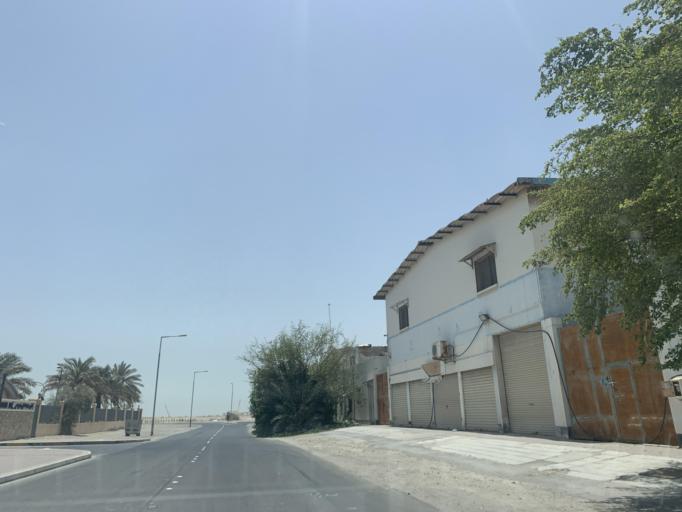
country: BH
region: Northern
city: Sitrah
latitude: 26.1560
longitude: 50.6244
